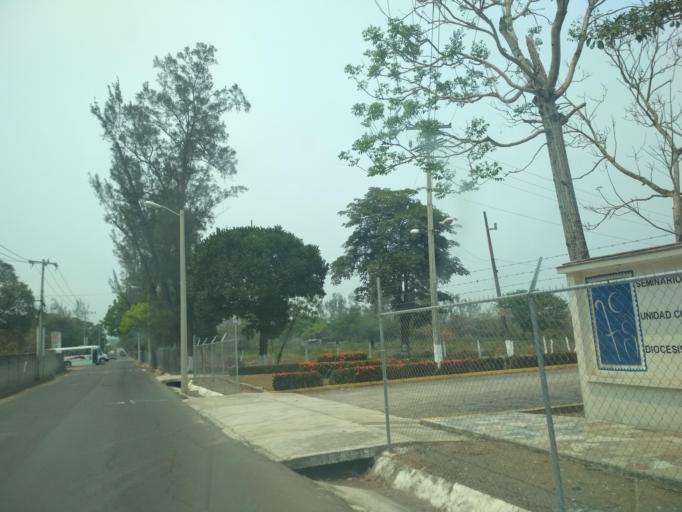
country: MX
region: Veracruz
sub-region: Veracruz
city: Las Amapolas
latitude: 19.1538
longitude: -96.2099
